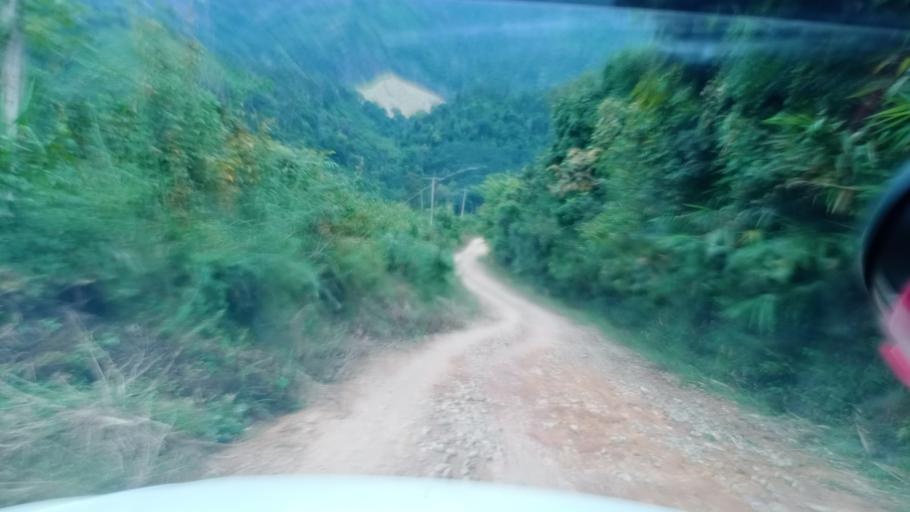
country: TH
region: Changwat Bueng Kan
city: Pak Khat
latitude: 18.7220
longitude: 103.2511
